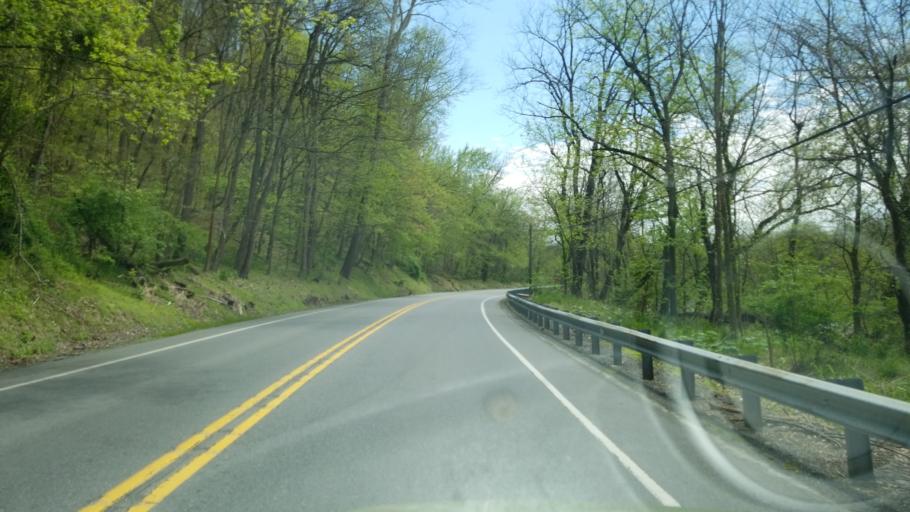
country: US
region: Pennsylvania
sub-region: Huntingdon County
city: Mount Union
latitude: 40.4018
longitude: -77.9383
